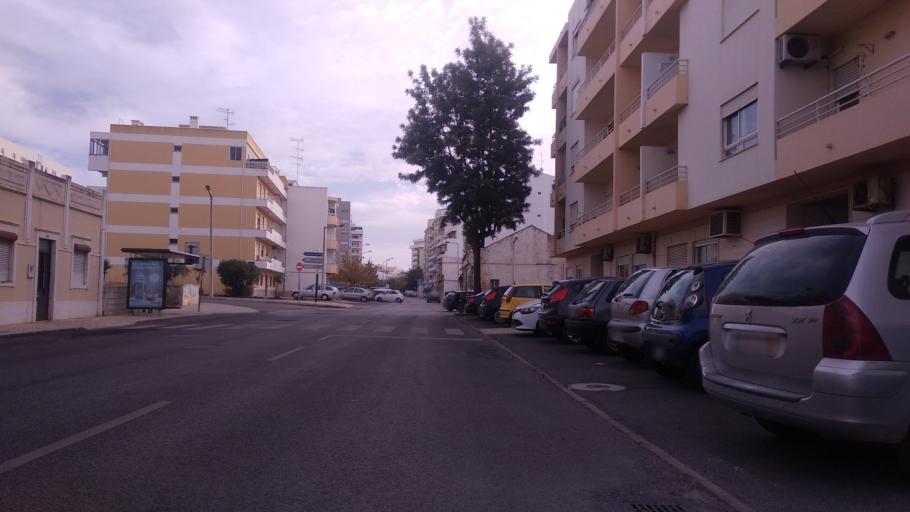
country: PT
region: Faro
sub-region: Faro
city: Faro
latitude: 37.0280
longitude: -7.9399
